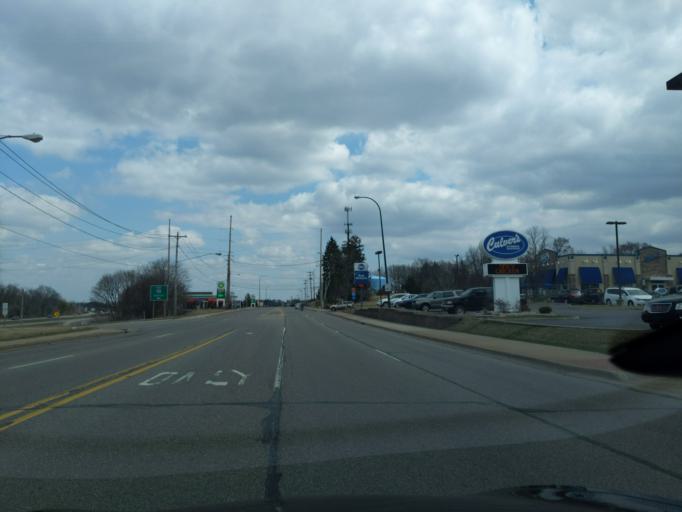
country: US
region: Michigan
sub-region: Calhoun County
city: Lakeview
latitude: 42.2610
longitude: -85.1977
